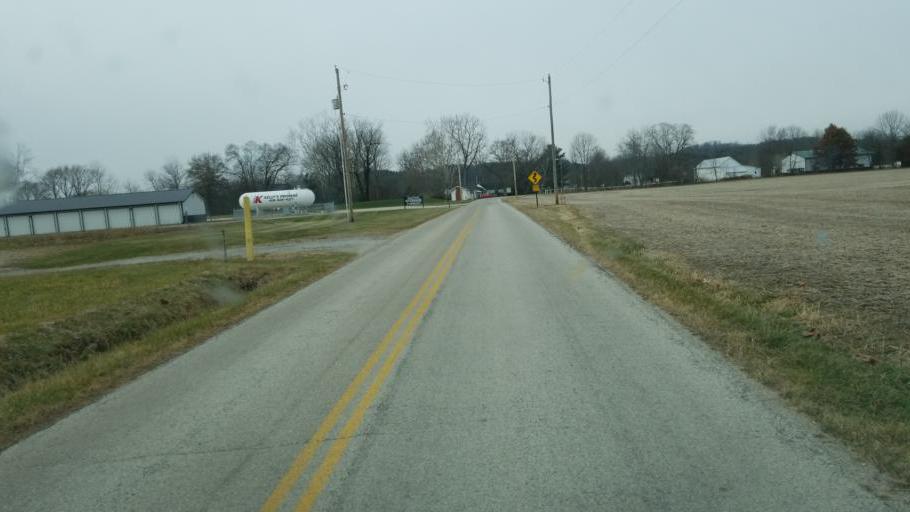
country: US
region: Ohio
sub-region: Sandusky County
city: Bellville
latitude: 40.6289
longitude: -82.5368
